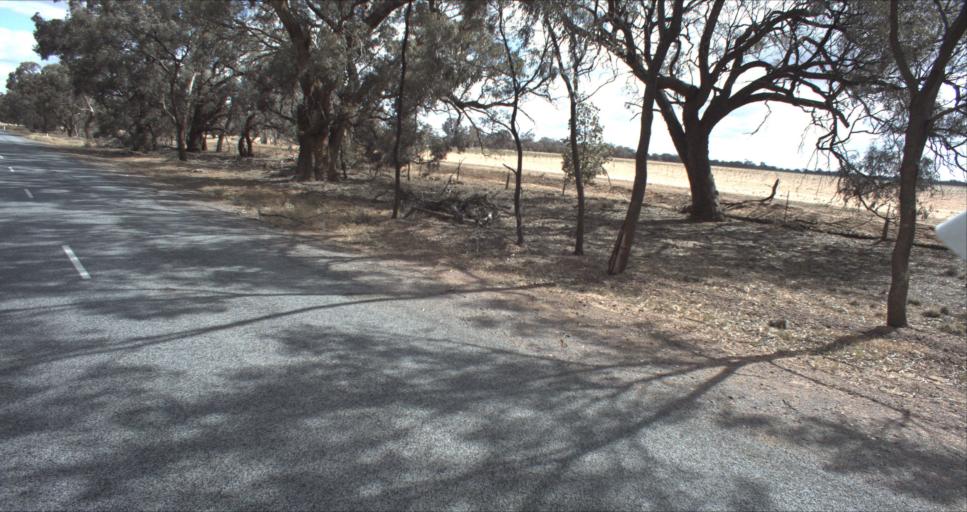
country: AU
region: New South Wales
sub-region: Leeton
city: Leeton
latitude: -34.6631
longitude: 146.3490
